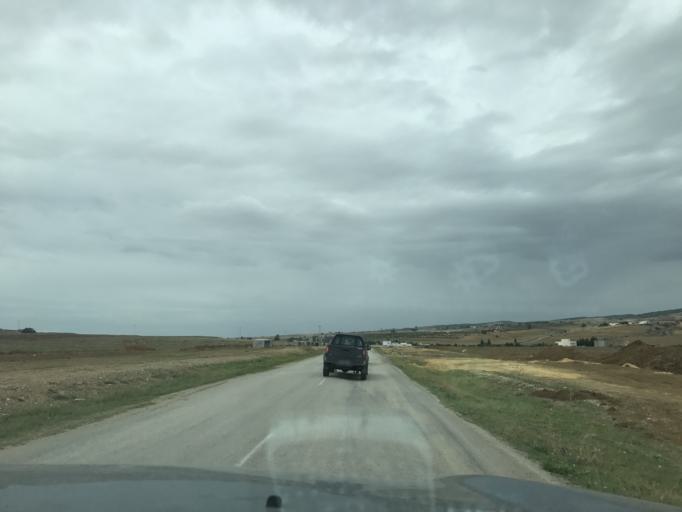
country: TN
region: Silyanah
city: Bu `Aradah
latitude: 36.2067
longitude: 9.7272
